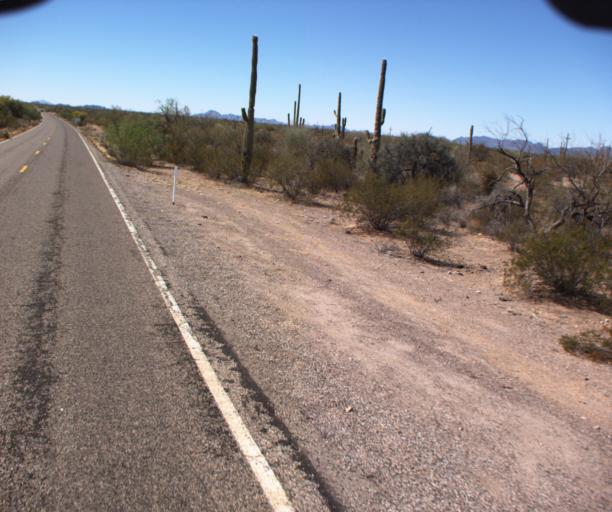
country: US
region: Arizona
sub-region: Pima County
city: Ajo
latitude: 32.2203
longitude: -112.7569
